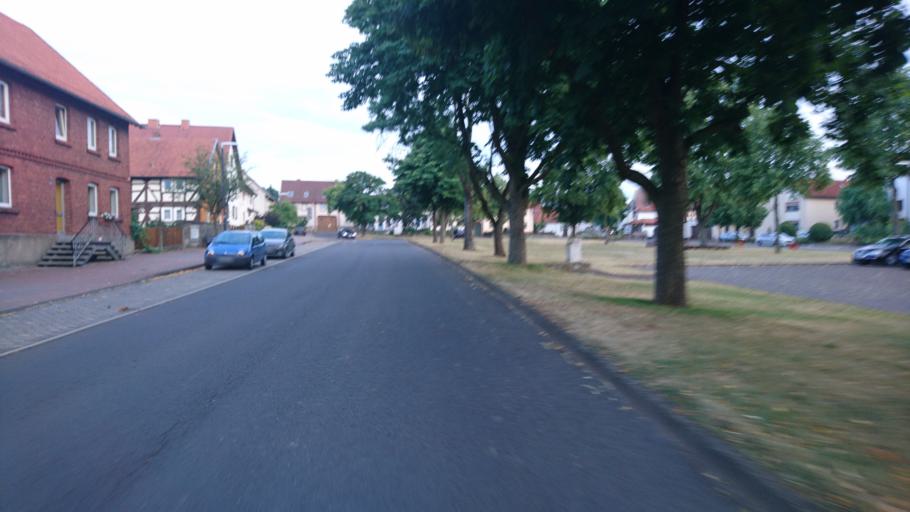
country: DE
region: Hesse
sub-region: Regierungsbezirk Kassel
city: Rasdorf
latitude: 50.7185
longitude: 9.8982
